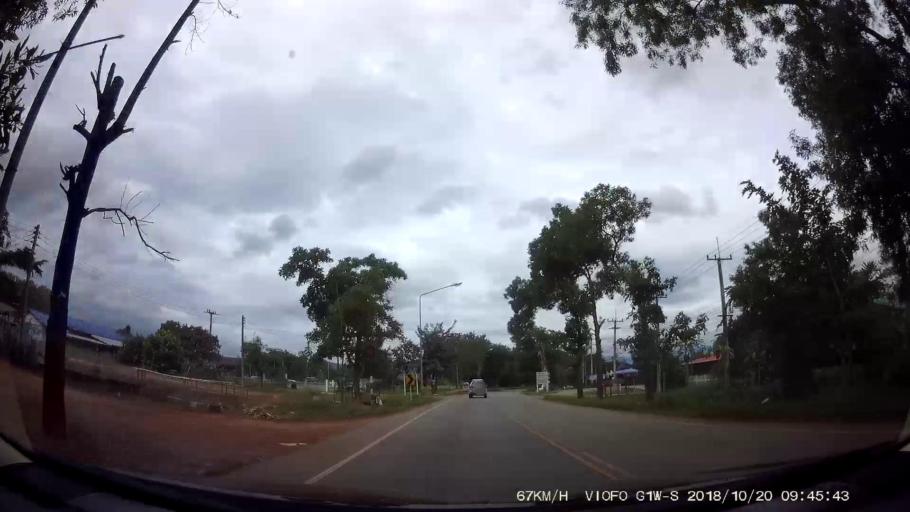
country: TH
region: Chaiyaphum
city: Khon San
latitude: 16.4914
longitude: 101.9327
